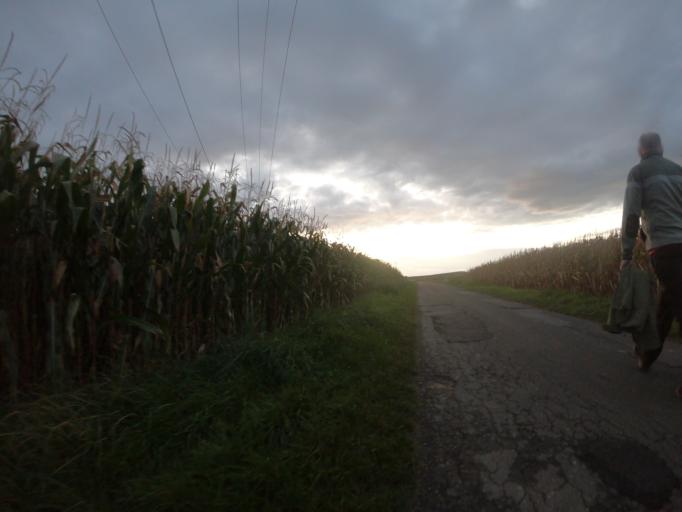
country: DE
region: Rheinland-Pfalz
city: Netzbach
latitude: 50.3303
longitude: 8.1664
